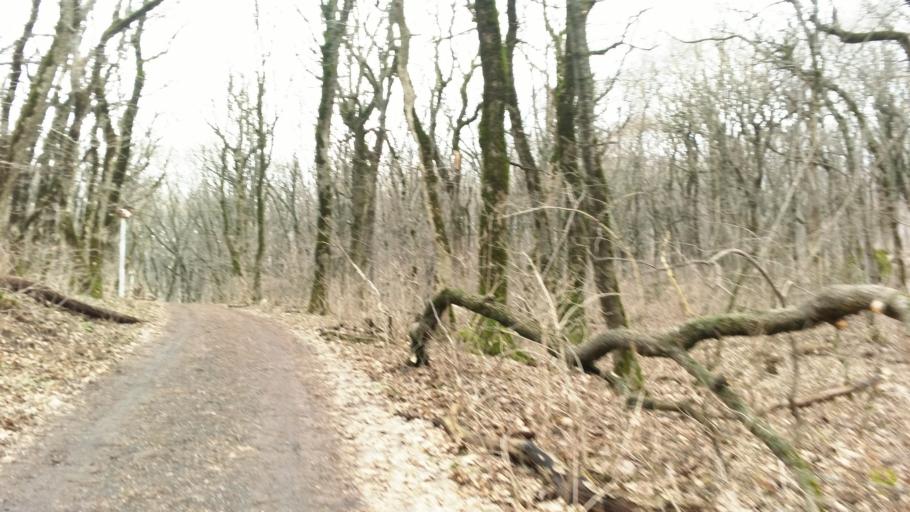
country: RU
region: Stavropol'skiy
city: Zheleznovodsk
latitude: 44.1588
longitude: 43.0405
